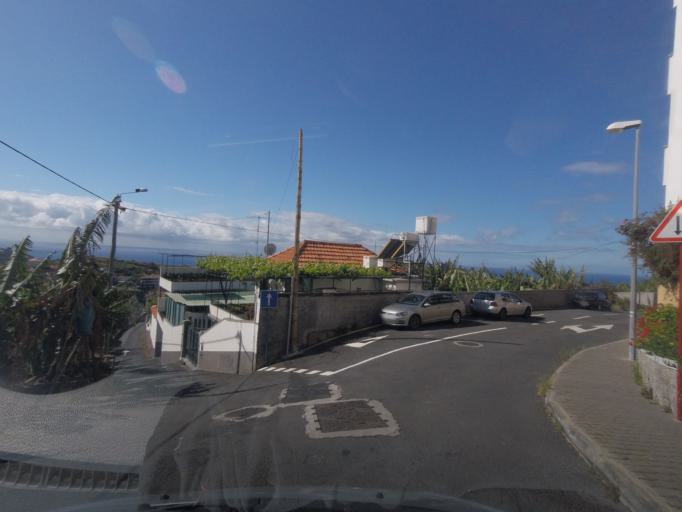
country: PT
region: Madeira
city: Camara de Lobos
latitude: 32.6592
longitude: -16.9727
